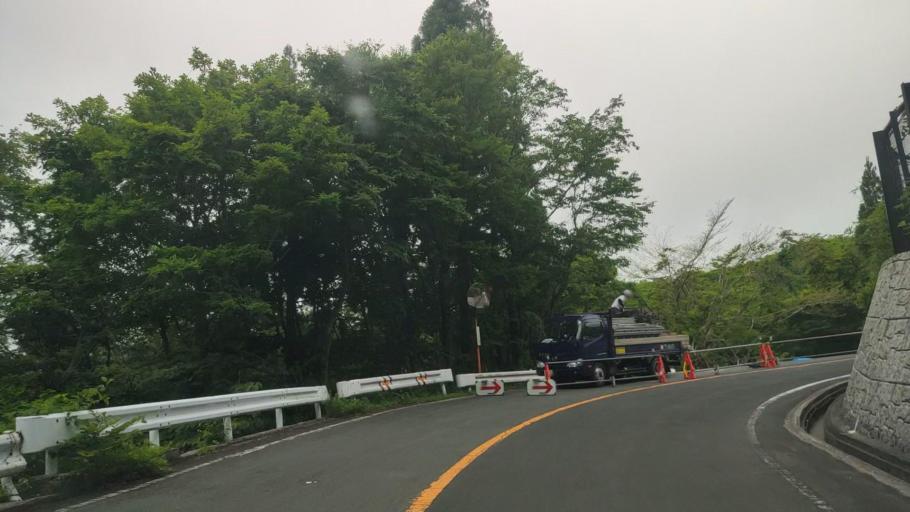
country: JP
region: Tottori
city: Yonago
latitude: 35.3510
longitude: 133.5480
